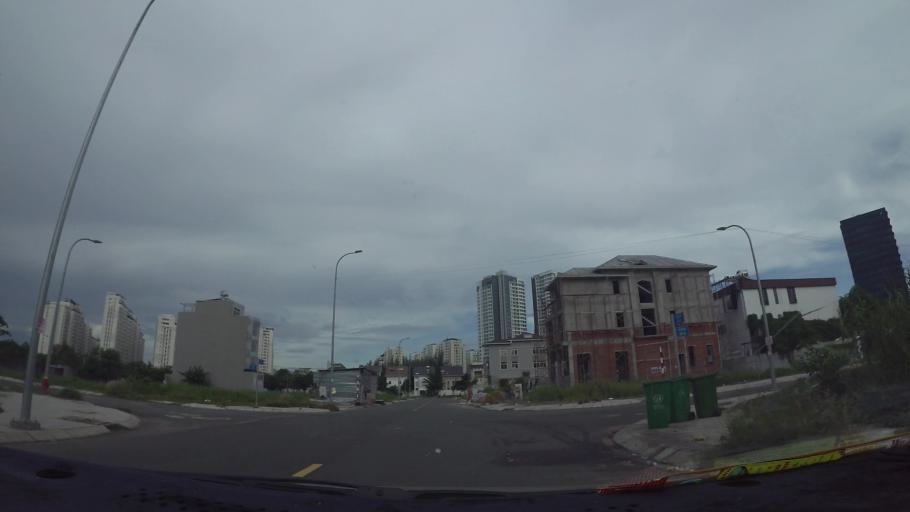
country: VN
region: Ho Chi Minh City
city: Quan Sau
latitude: 10.7441
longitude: 106.6526
